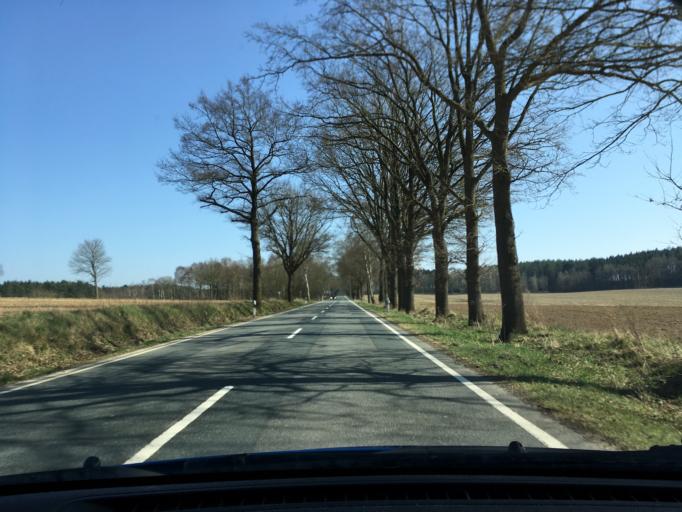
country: DE
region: Lower Saxony
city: Rehlingen
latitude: 53.1156
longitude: 10.2316
